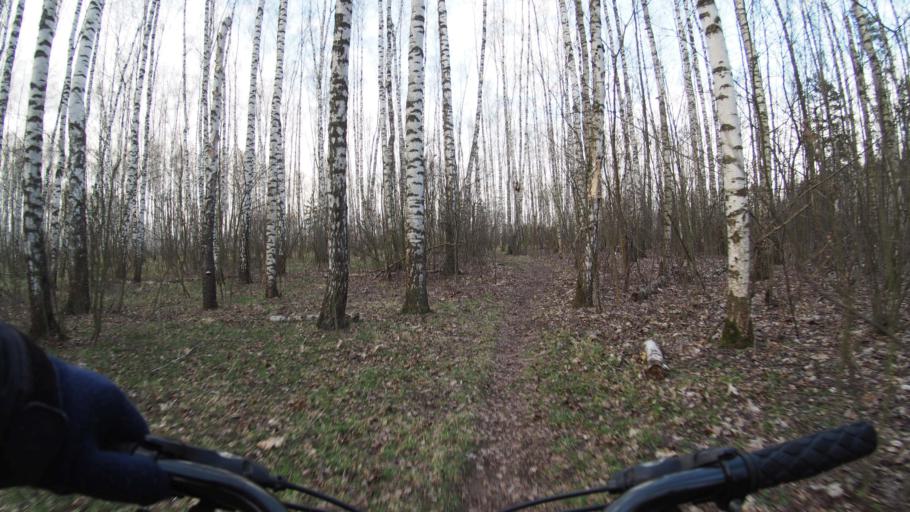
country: RU
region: Moskovskaya
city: Malyshevo
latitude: 55.5197
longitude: 38.3079
